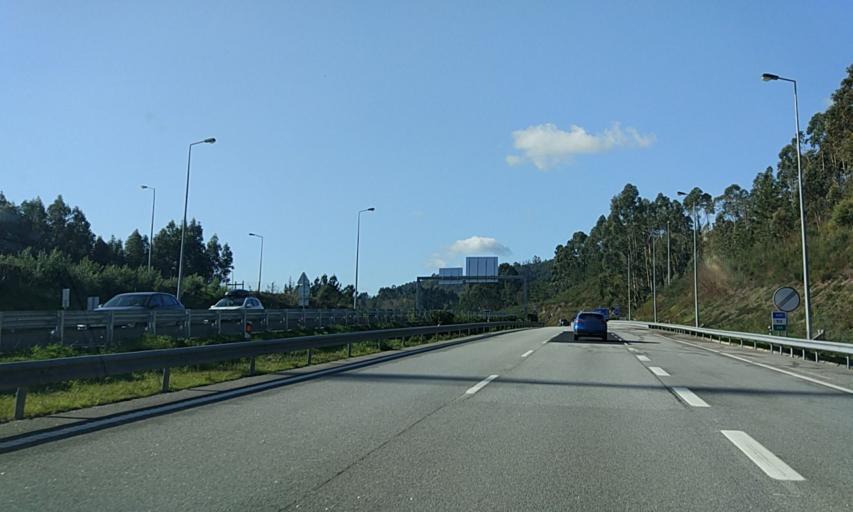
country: PT
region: Viseu
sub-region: Oliveira de Frades
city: Oliveira de Frades
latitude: 40.6815
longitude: -8.2678
